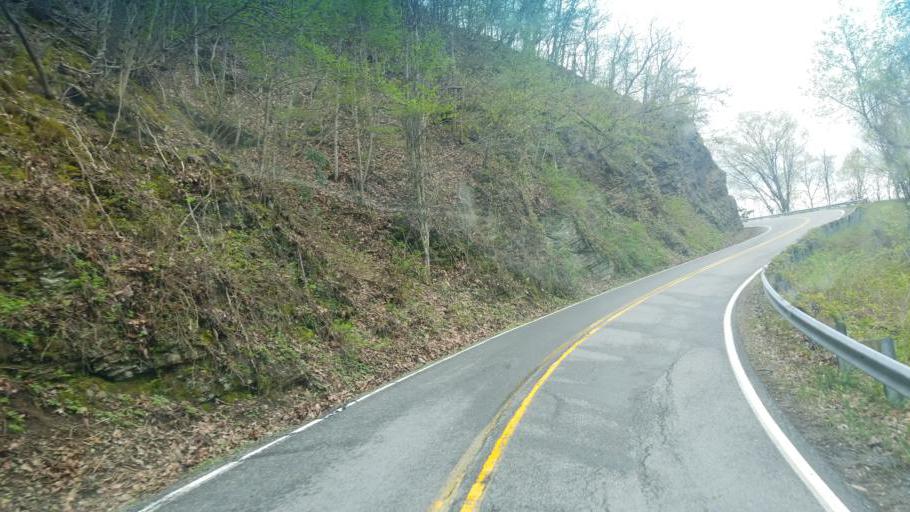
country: US
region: Virginia
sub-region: Tazewell County
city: Tazewell
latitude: 36.9998
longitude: -81.5314
